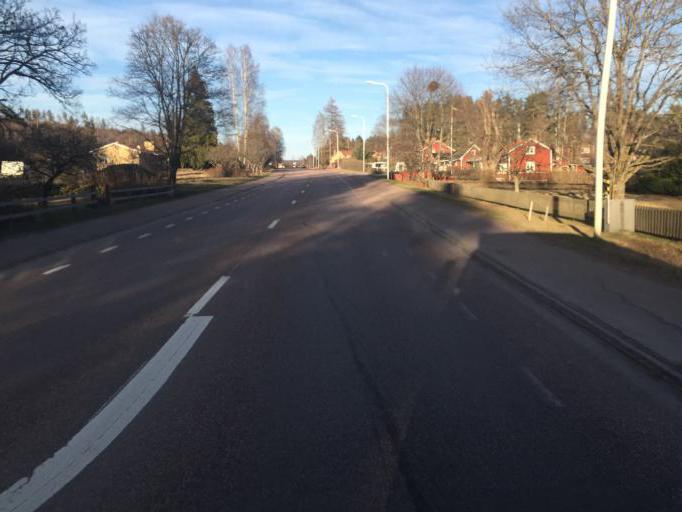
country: SE
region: Dalarna
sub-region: Gagnefs Kommun
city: Djuras
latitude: 60.5512
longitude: 15.1894
